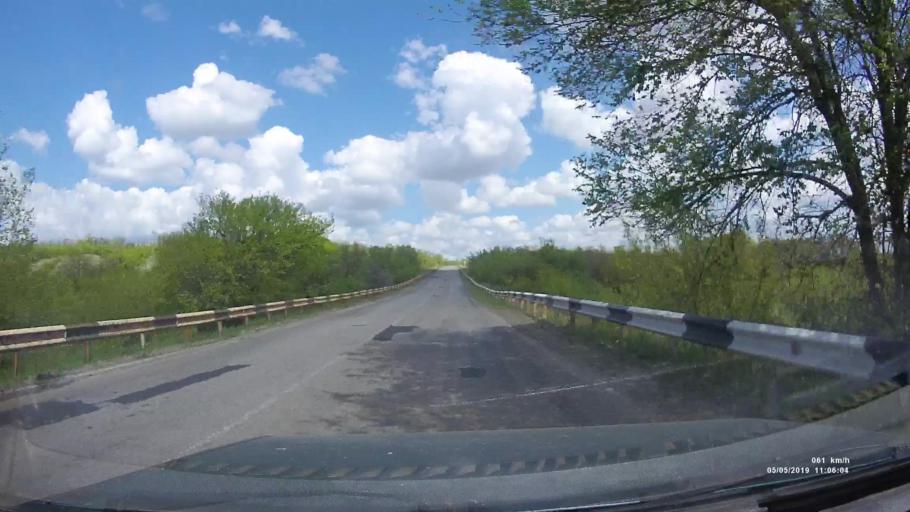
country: RU
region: Rostov
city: Ust'-Donetskiy
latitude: 47.7111
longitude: 40.9112
